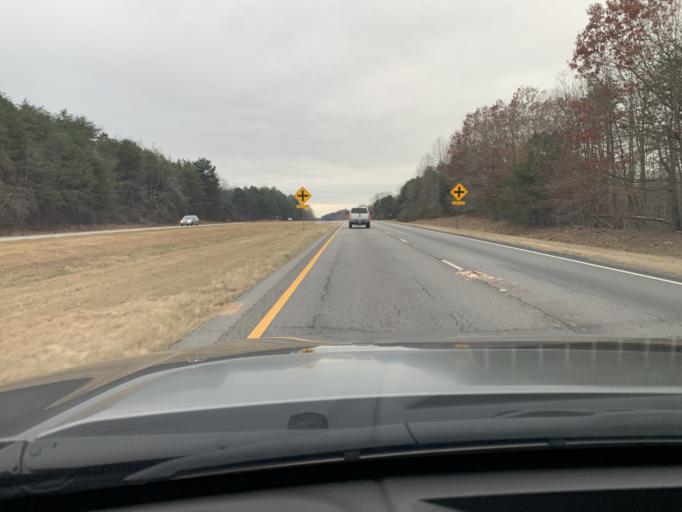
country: US
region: Georgia
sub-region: Habersham County
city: Raoul
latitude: 34.4702
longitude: -83.5975
